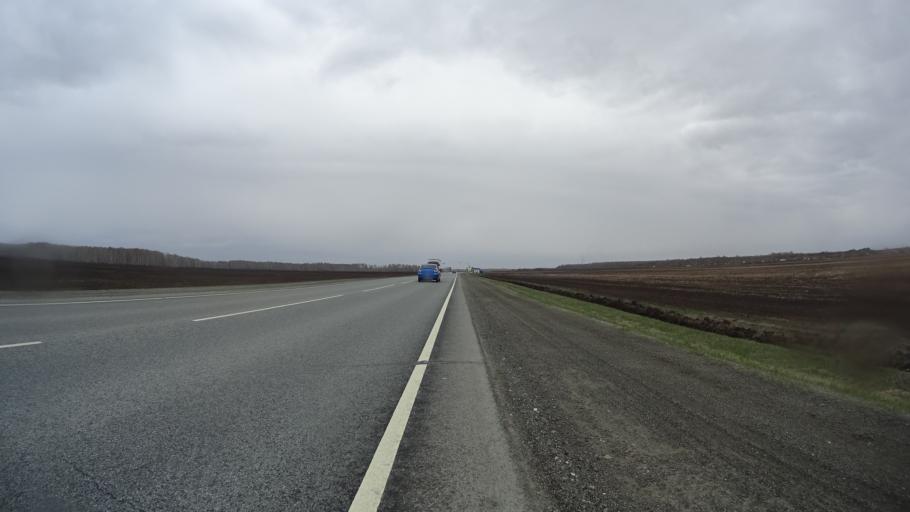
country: RU
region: Chelyabinsk
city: Krasnogorskiy
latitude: 54.5843
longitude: 61.2909
